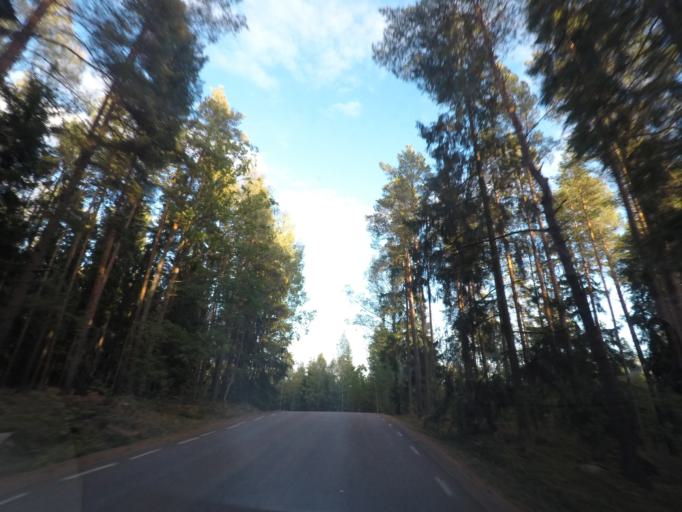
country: SE
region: Vaestmanland
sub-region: Kungsors Kommun
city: Kungsoer
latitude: 59.5094
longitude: 16.0842
